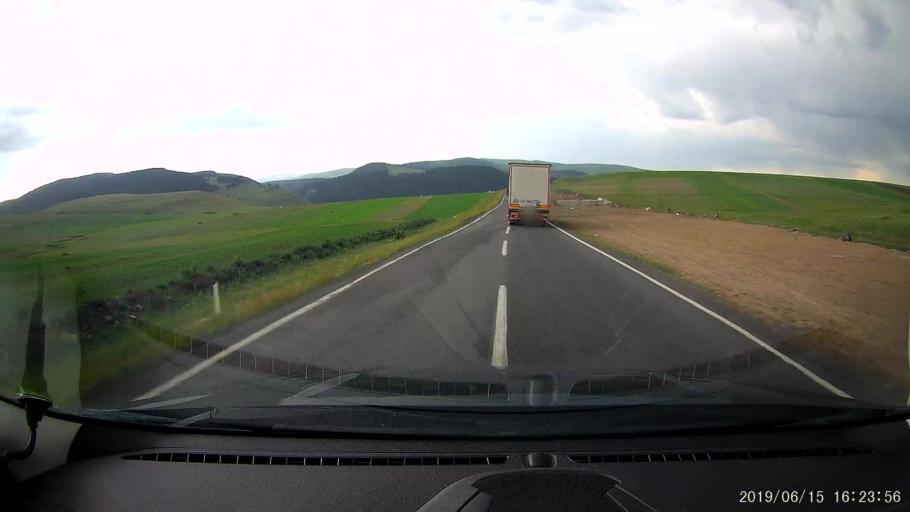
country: TR
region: Ardahan
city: Hanak
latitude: 41.1718
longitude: 42.8671
